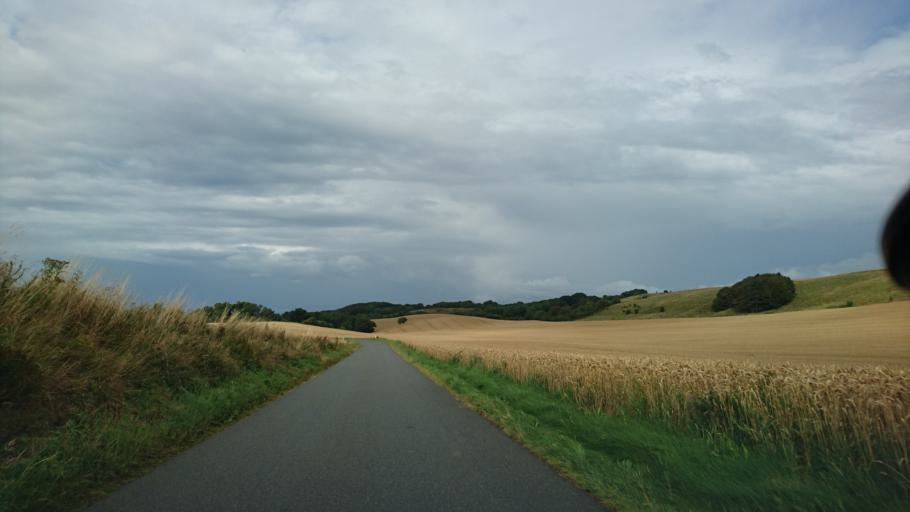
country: DK
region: North Denmark
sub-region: Frederikshavn Kommune
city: Saeby
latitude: 57.3890
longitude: 10.4769
